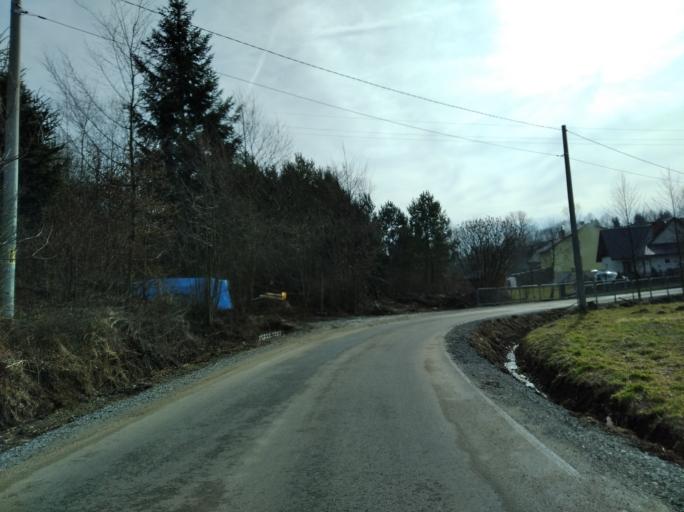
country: PL
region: Subcarpathian Voivodeship
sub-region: Powiat brzozowski
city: Jasienica Rosielna
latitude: 49.7680
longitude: 21.9427
